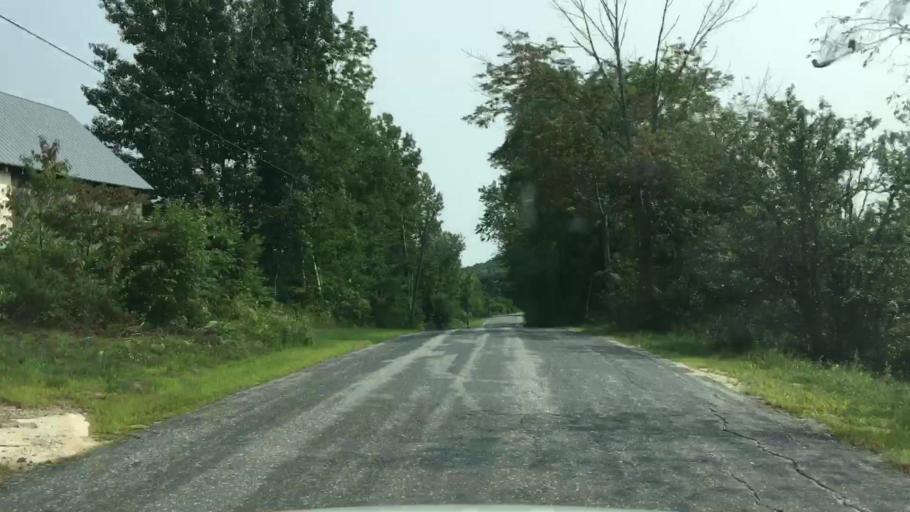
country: US
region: Maine
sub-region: Androscoggin County
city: Turner
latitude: 44.3202
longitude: -70.2894
